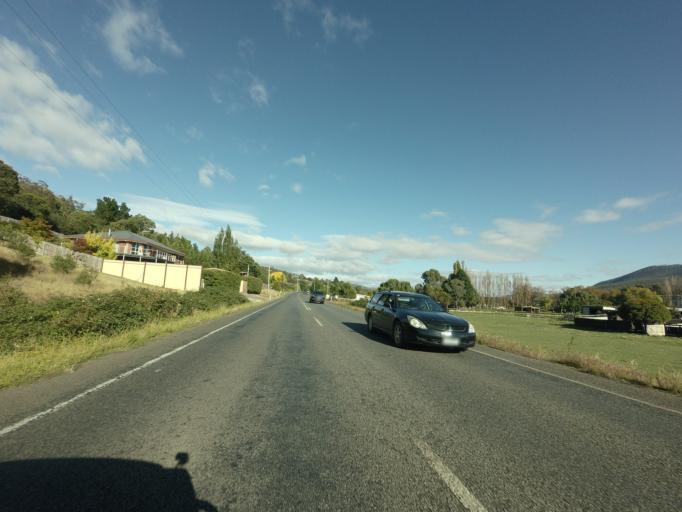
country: AU
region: Tasmania
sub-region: Derwent Valley
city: New Norfolk
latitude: -42.7839
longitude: 147.1032
